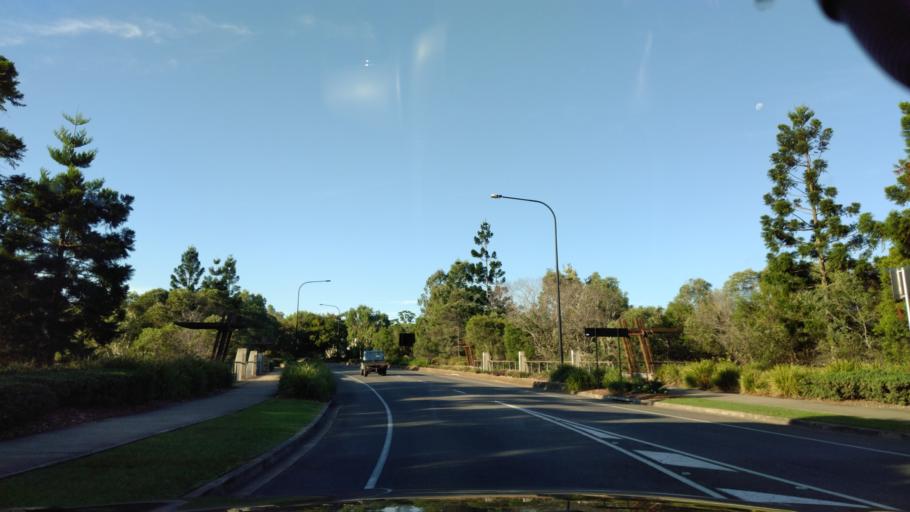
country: AU
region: Queensland
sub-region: Moreton Bay
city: Mango Hill
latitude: -27.2224
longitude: 153.0222
